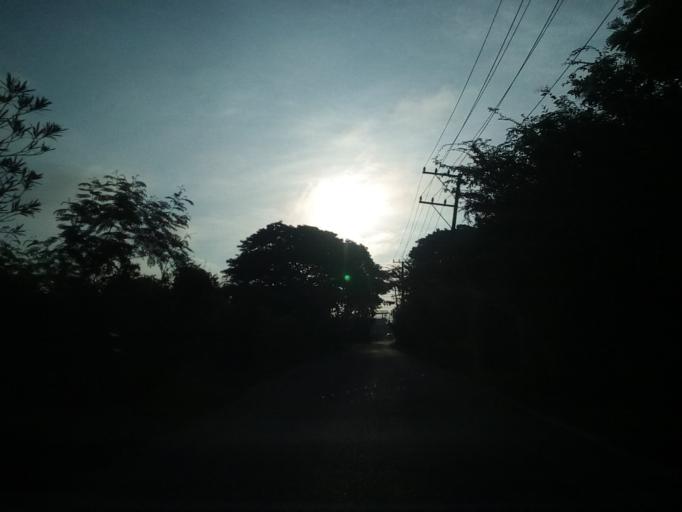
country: TH
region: Lamphun
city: Ban Thi
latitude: 18.6347
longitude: 99.0492
